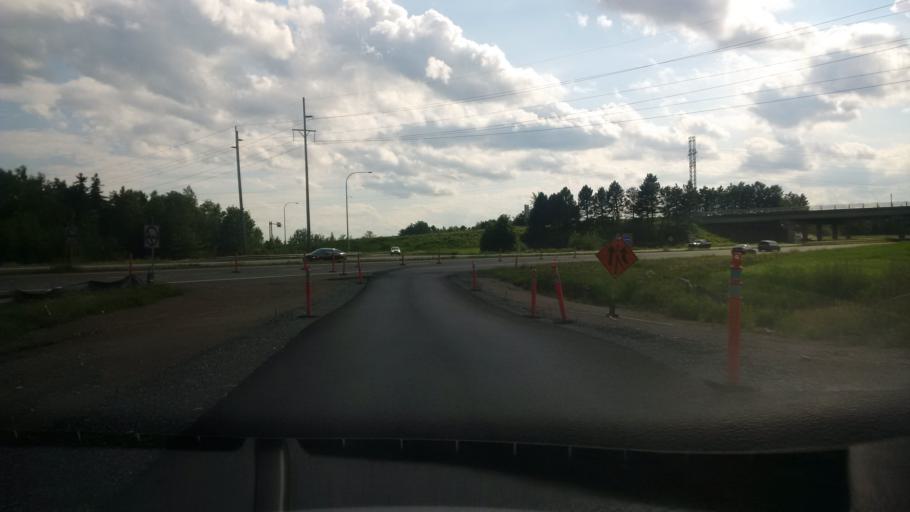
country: CA
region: New Brunswick
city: Fredericton
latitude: 45.9359
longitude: -66.6508
